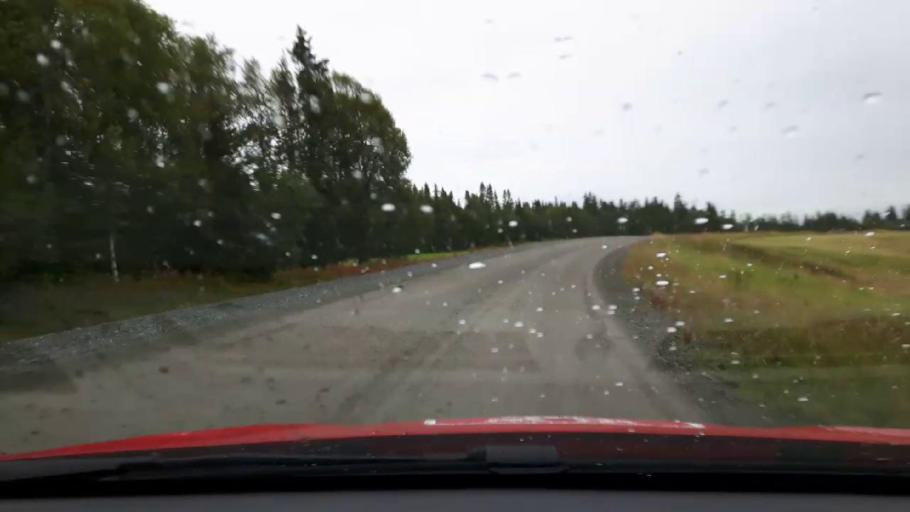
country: SE
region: Jaemtland
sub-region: Are Kommun
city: Are
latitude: 63.4724
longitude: 12.5729
